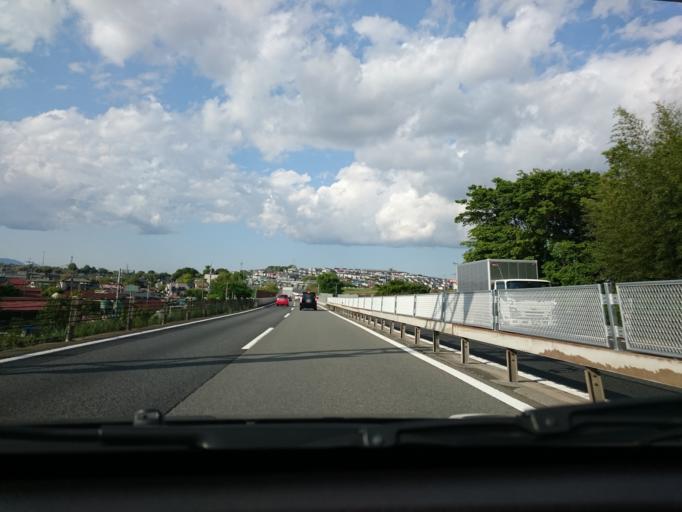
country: JP
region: Kanagawa
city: Oiso
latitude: 35.3332
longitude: 139.2933
